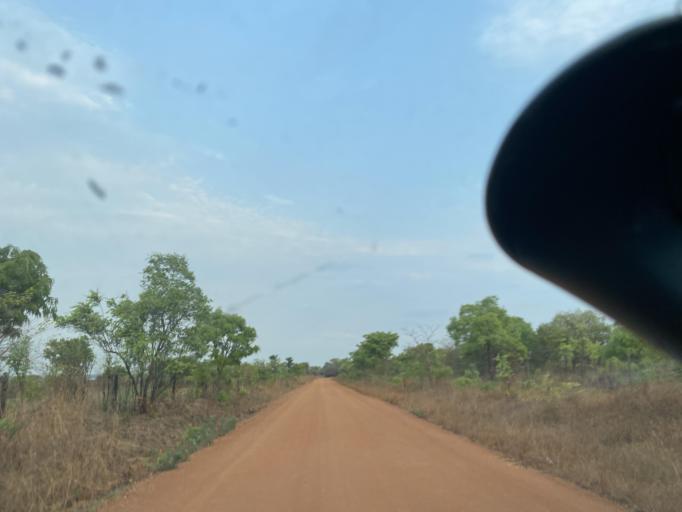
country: ZM
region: Lusaka
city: Chongwe
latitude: -15.2227
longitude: 28.5888
